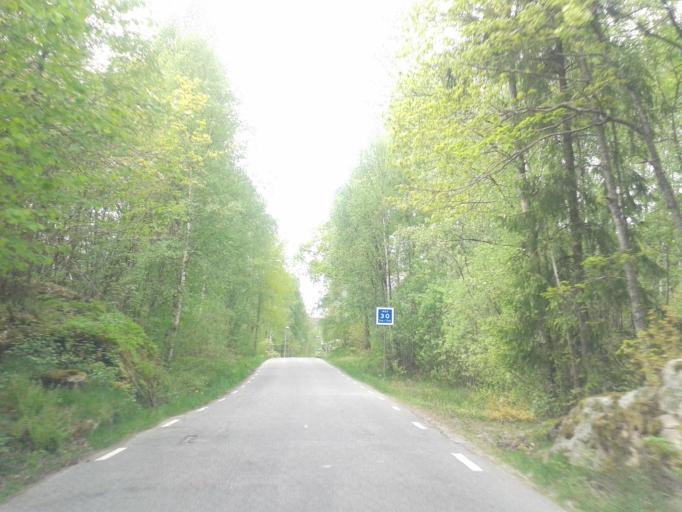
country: SE
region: Vaestra Goetaland
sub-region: Kungalvs Kommun
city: Kungalv
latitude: 57.8567
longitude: 11.9346
